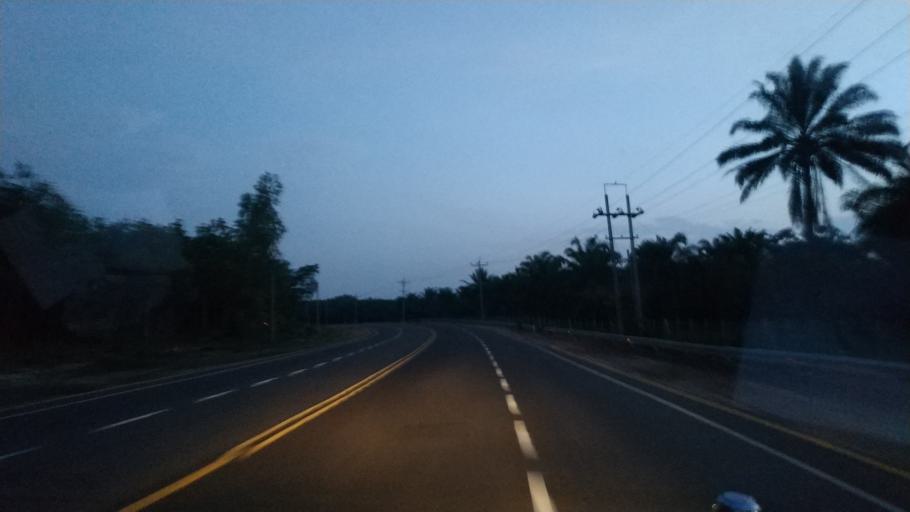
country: MM
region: Mon
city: Kyaikto
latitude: 17.3716
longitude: 97.0500
